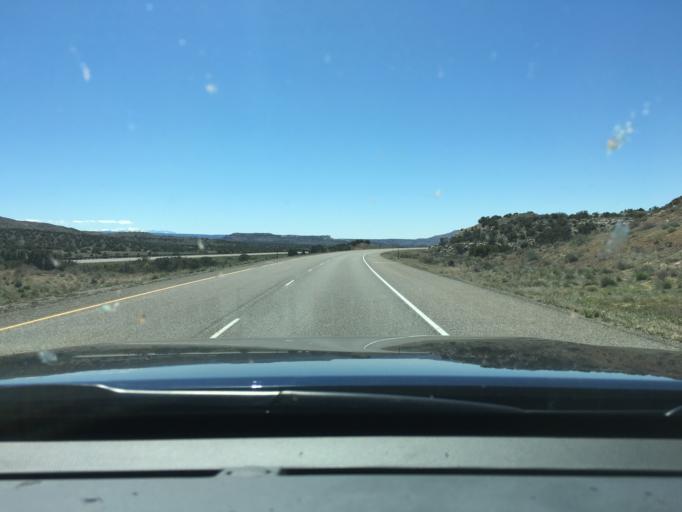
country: US
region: Colorado
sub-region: Mesa County
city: Loma
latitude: 39.2140
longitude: -108.9658
